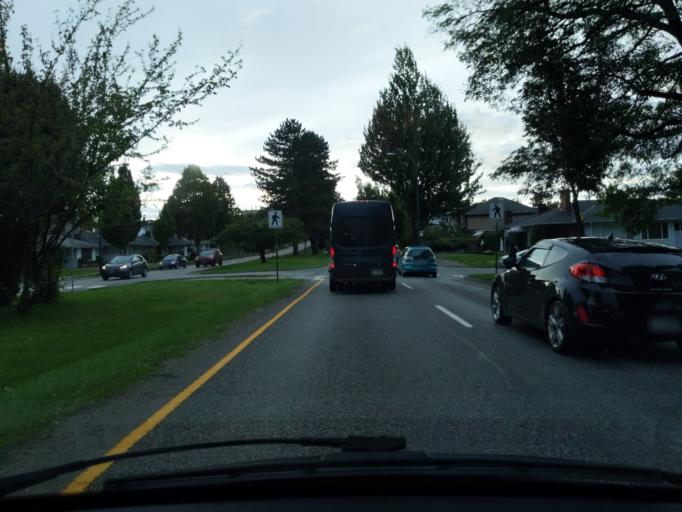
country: CA
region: British Columbia
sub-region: Fraser Valley Regional District
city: North Vancouver
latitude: 49.2696
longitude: -123.0516
